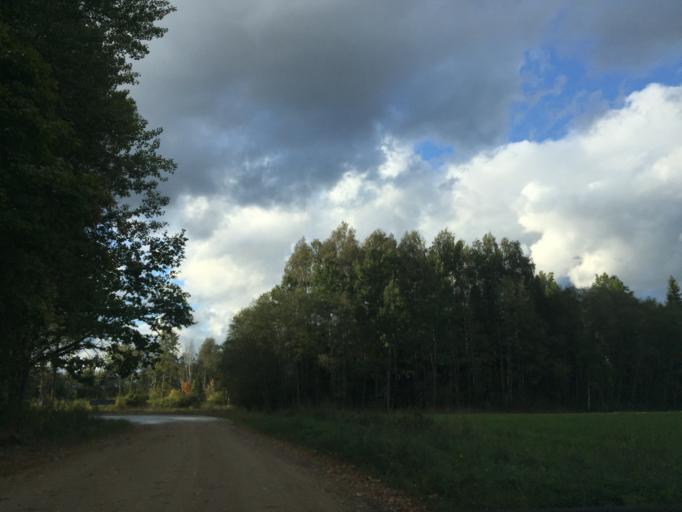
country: LV
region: Ligatne
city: Ligatne
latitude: 57.1384
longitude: 25.0833
